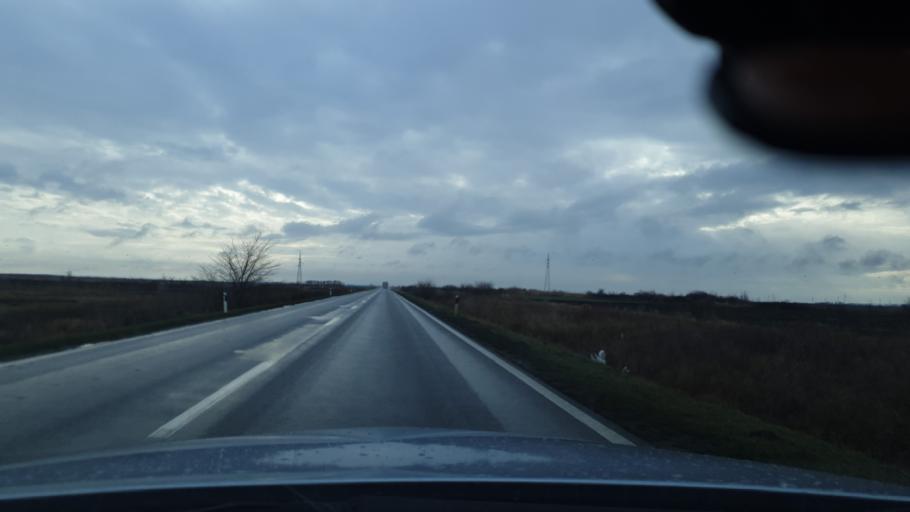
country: RS
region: Autonomna Pokrajina Vojvodina
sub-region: Juznobanatski Okrug
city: Kovin
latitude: 44.7990
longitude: 20.9051
